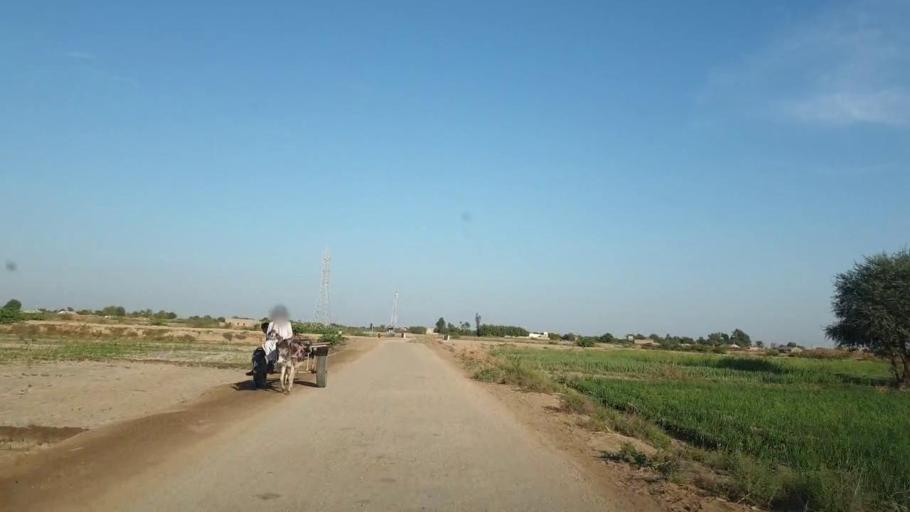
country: PK
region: Sindh
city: Kunri
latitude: 25.0911
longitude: 69.4278
